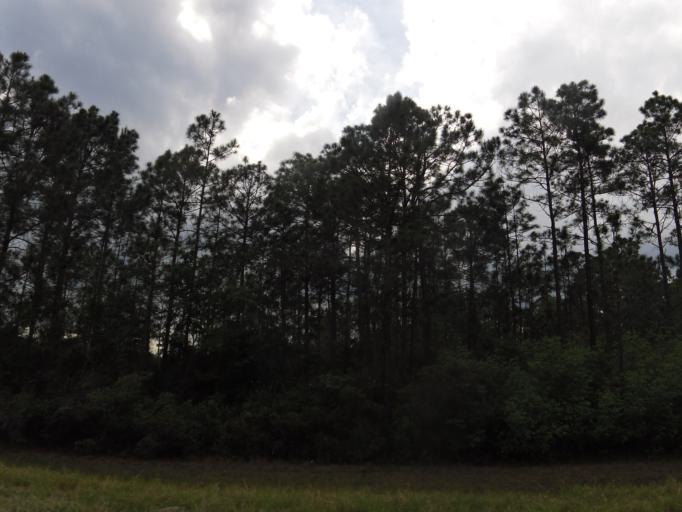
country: US
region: Georgia
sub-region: Charlton County
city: Folkston
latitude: 30.8751
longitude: -82.0151
